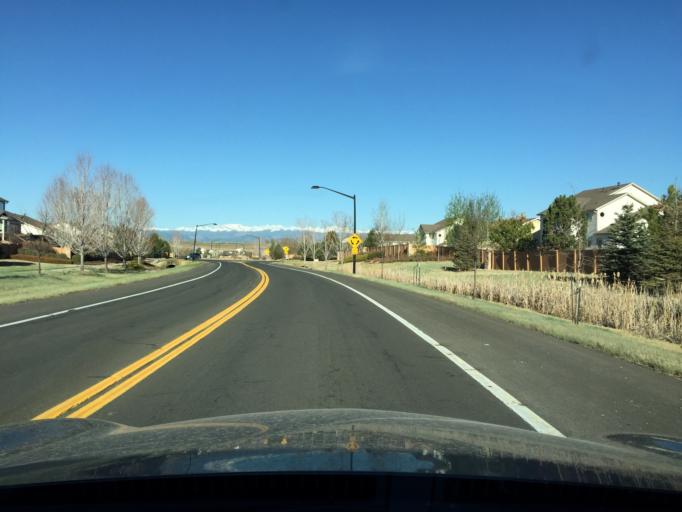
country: US
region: Colorado
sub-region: Boulder County
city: Erie
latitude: 40.0209
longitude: -105.0403
